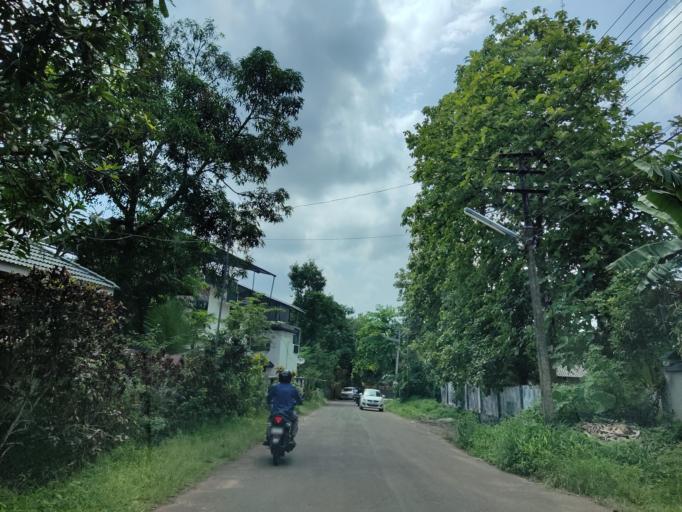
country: IN
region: Kerala
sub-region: Alappuzha
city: Mavelikara
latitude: 9.2546
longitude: 76.5670
